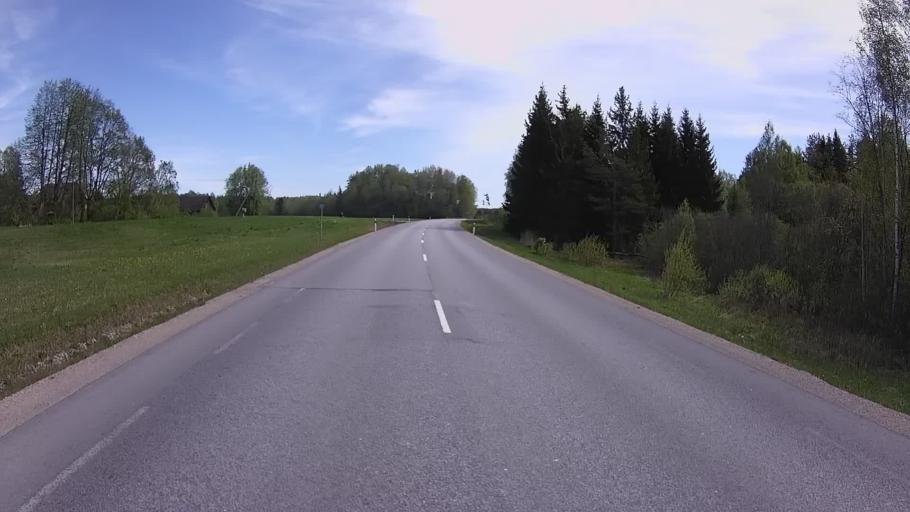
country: EE
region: Valgamaa
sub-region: Valga linn
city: Valga
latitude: 57.7100
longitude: 26.2302
